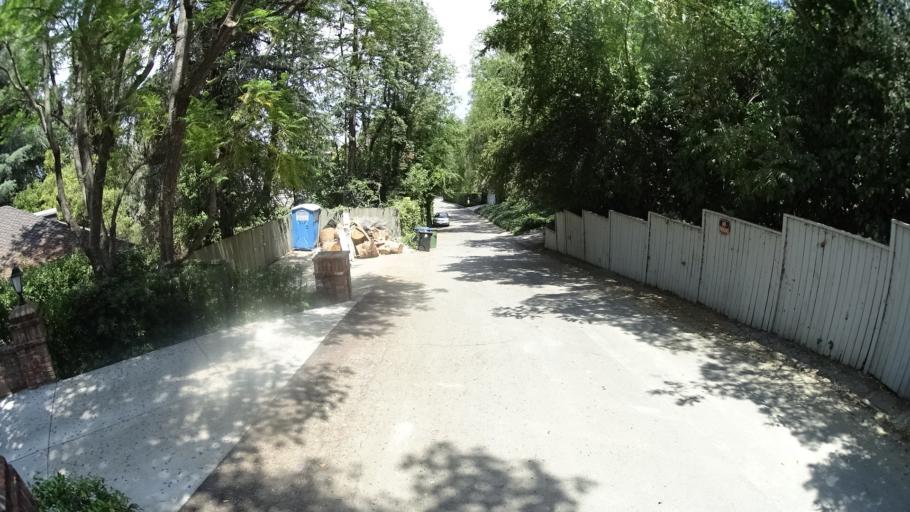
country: US
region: California
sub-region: Los Angeles County
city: Sherman Oaks
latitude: 34.1424
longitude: -118.4221
